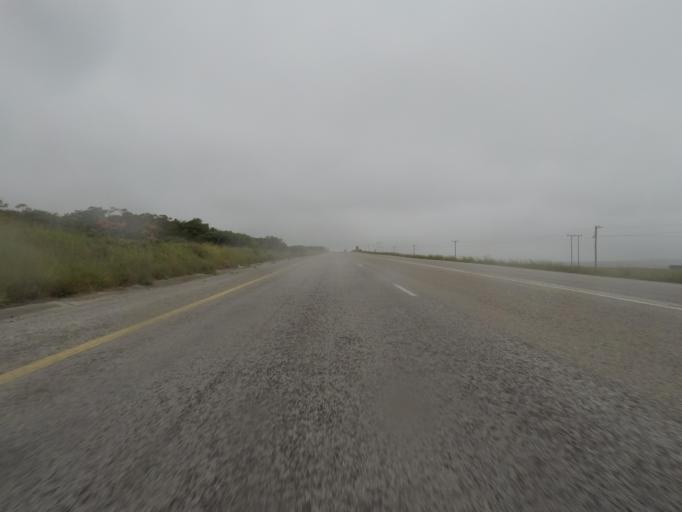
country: ZA
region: Eastern Cape
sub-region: Cacadu District Municipality
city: Grahamstown
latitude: -33.6246
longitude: 26.2981
